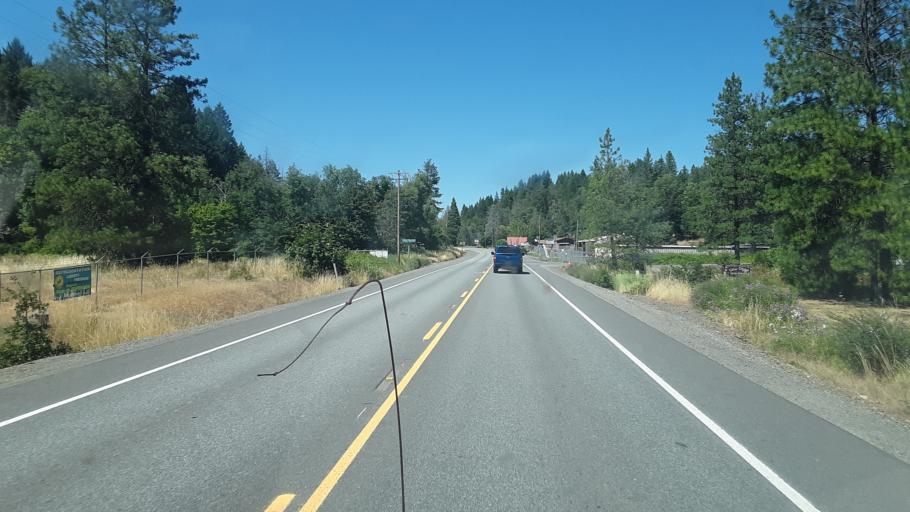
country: US
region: Oregon
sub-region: Josephine County
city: Cave Junction
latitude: 42.2865
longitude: -123.6133
